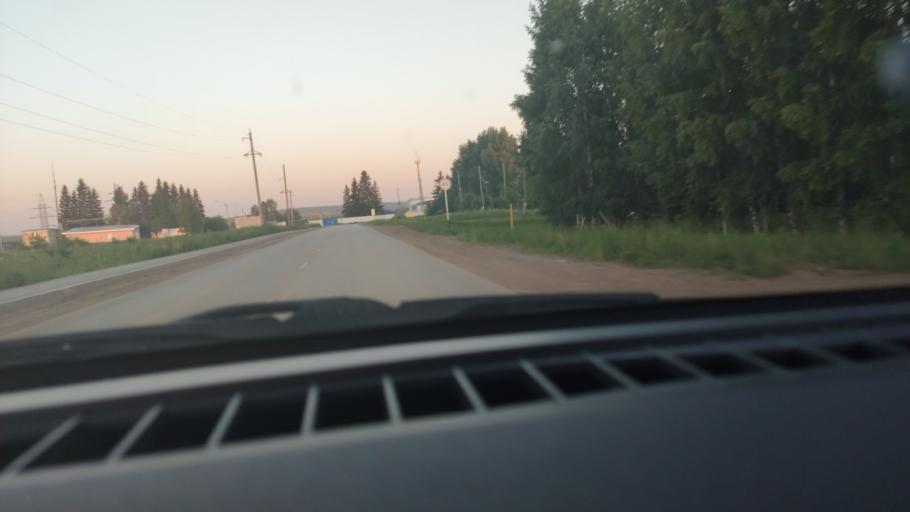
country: RU
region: Perm
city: Kultayevo
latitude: 57.8893
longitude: 55.9221
